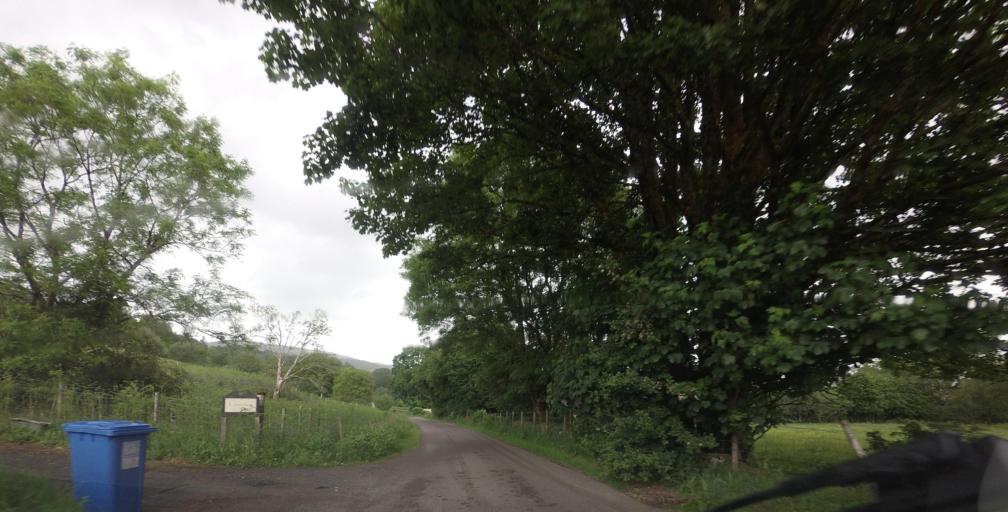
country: GB
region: Scotland
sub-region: Argyll and Bute
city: Oban
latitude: 56.7025
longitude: -5.5700
